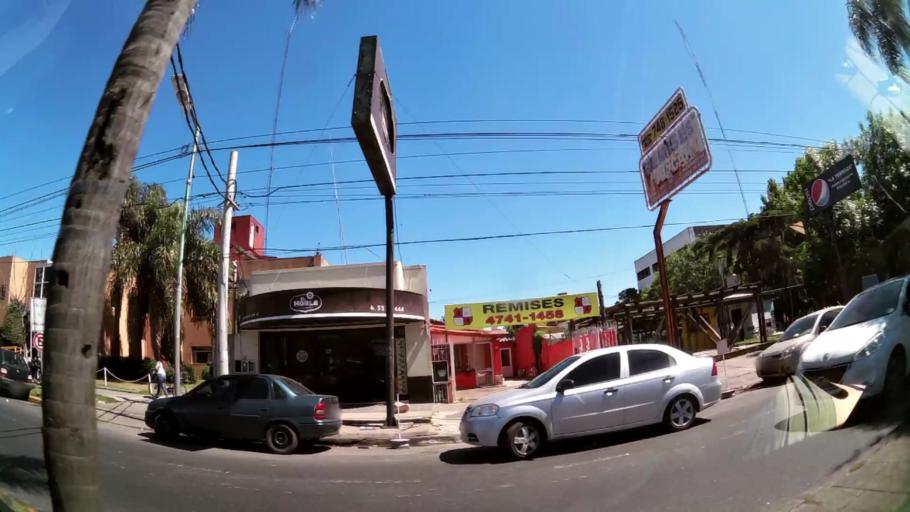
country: AR
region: Buenos Aires
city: Hurlingham
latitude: -34.4989
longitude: -58.6403
